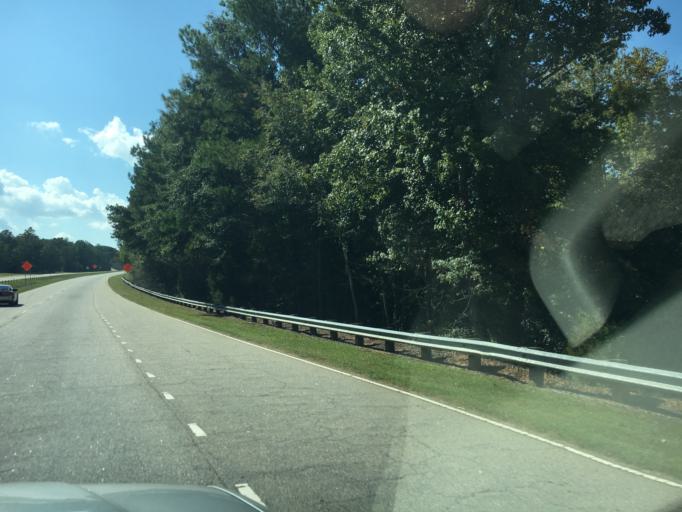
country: US
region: South Carolina
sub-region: Anderson County
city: Pendleton
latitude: 34.6869
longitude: -82.7931
